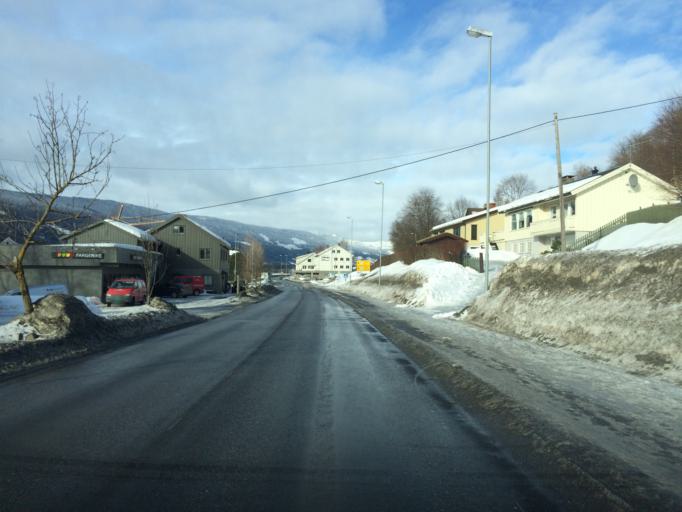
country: NO
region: Oppland
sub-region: Gausdal
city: Segalstad bru
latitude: 61.2276
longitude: 10.2247
